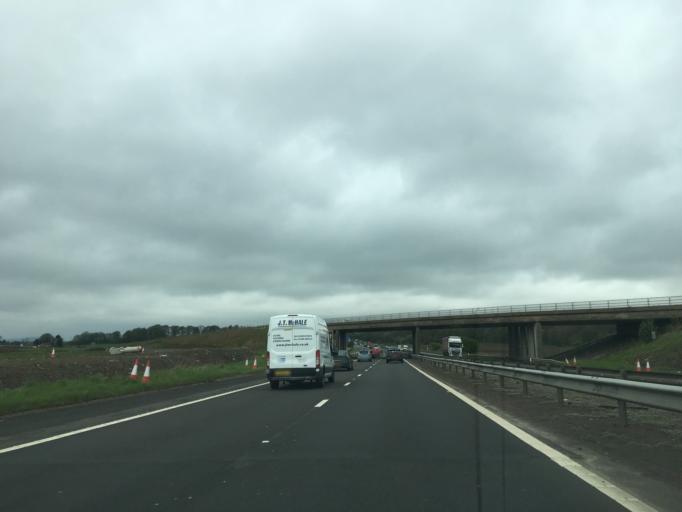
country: GB
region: Scotland
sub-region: Renfrewshire
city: Bishopton
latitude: 55.8911
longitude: -4.4807
